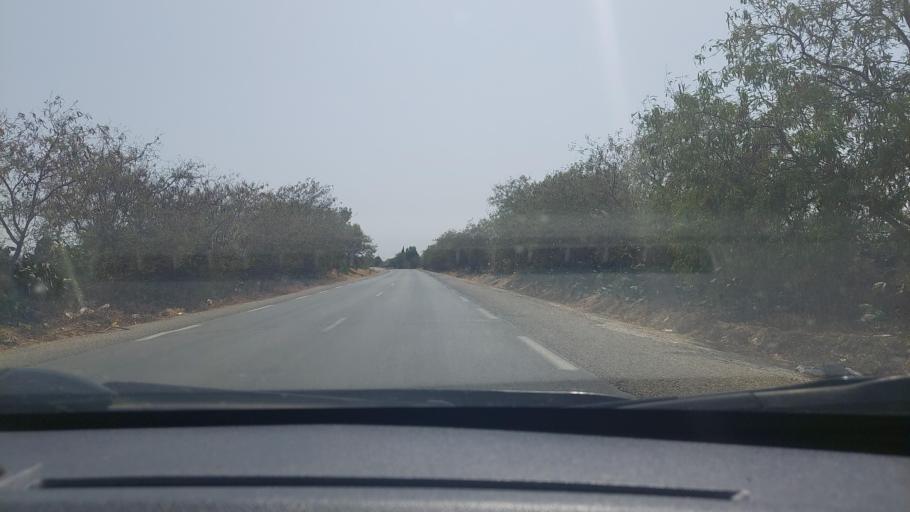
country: TN
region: Al Munastir
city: Sidi Bin Nur
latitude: 35.5695
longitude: 10.9107
